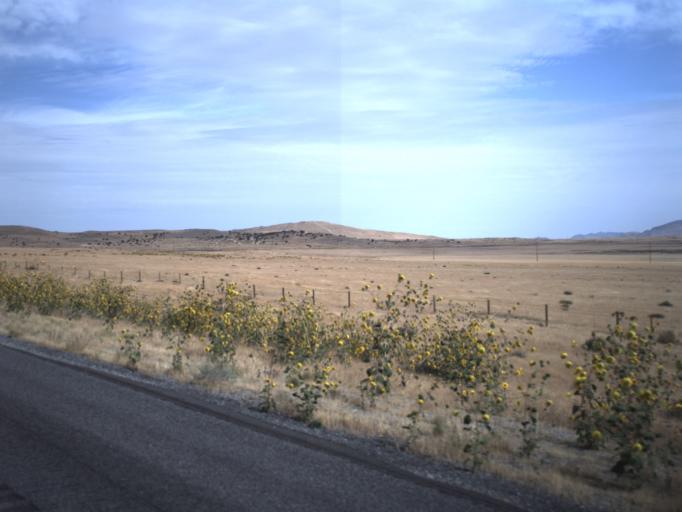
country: US
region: Utah
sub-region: Tooele County
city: Grantsville
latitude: 40.8172
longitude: -112.8805
